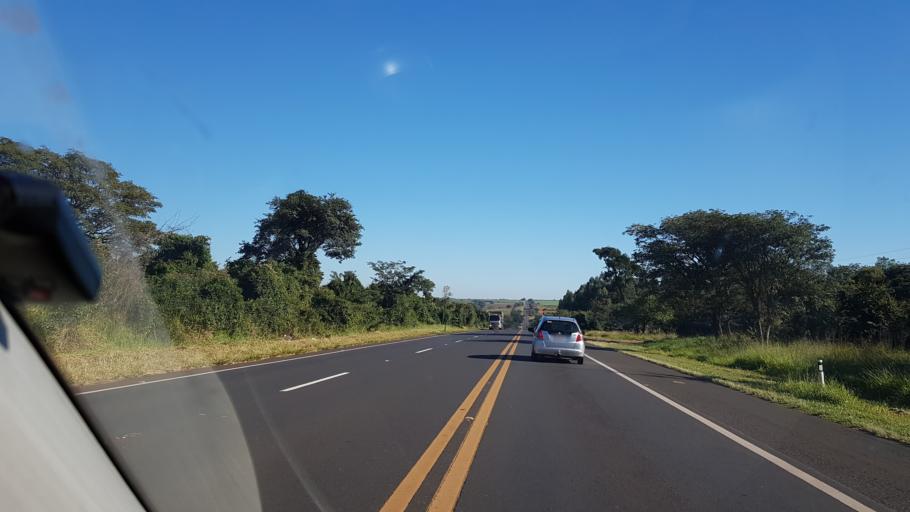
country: BR
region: Sao Paulo
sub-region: Assis
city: Assis
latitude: -22.6167
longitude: -50.4588
